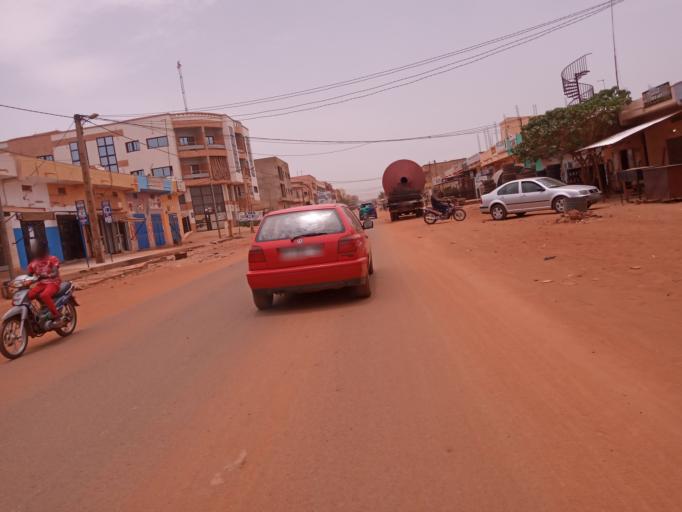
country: ML
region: Bamako
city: Bamako
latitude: 12.5811
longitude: -8.0193
